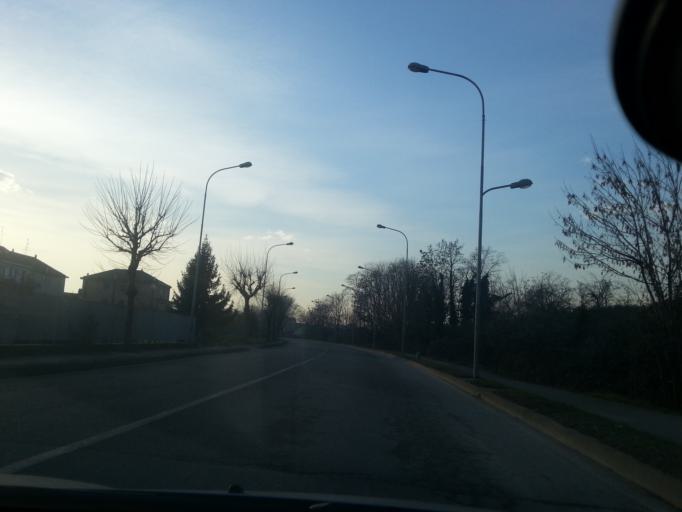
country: IT
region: Lombardy
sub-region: Citta metropolitana di Milano
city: Bollate
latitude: 45.5482
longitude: 9.1344
